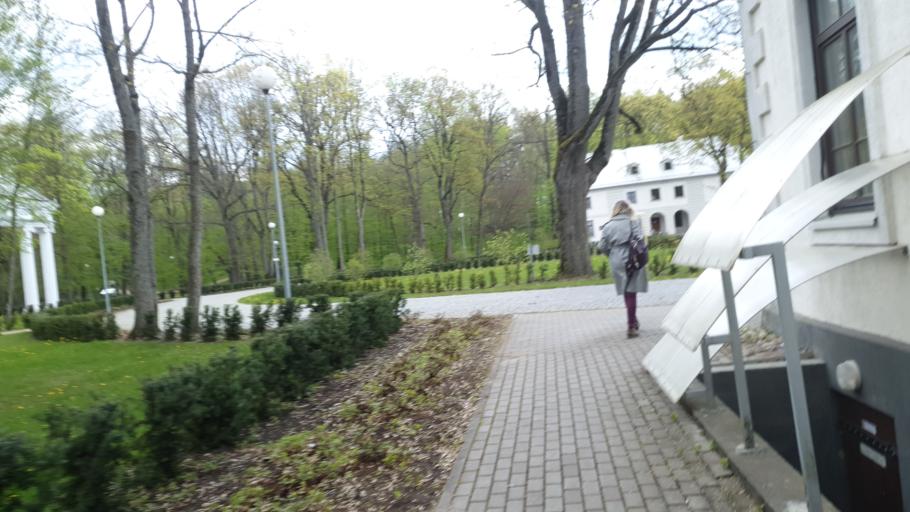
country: LT
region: Taurages apskritis
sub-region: Jurbarkas
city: Jurbarkas
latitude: 55.0788
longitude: 22.7566
